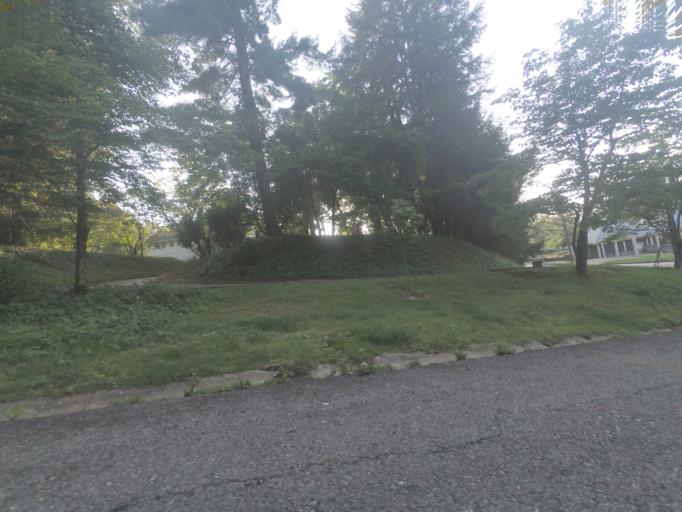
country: US
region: West Virginia
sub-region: Cabell County
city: Huntington
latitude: 38.4056
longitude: -82.4399
